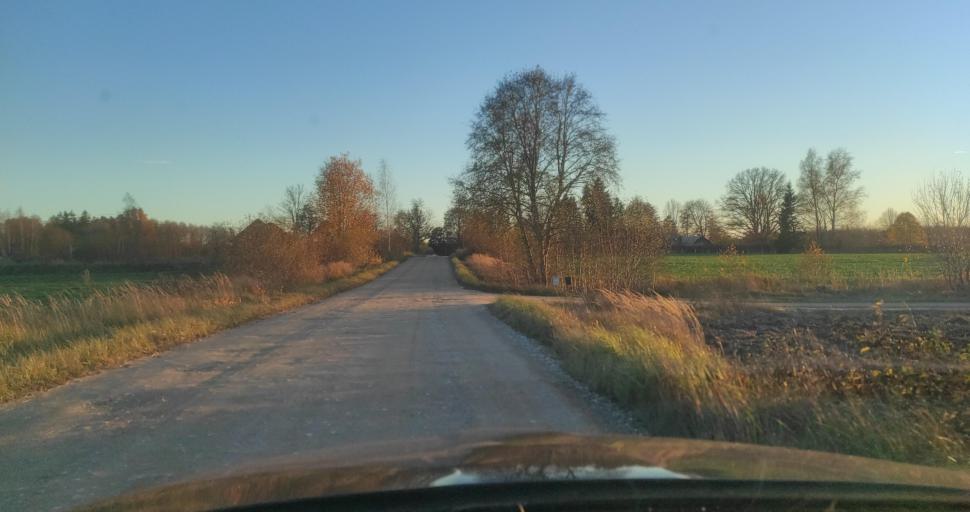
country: LV
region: Saldus Rajons
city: Saldus
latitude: 56.8060
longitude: 22.2850
